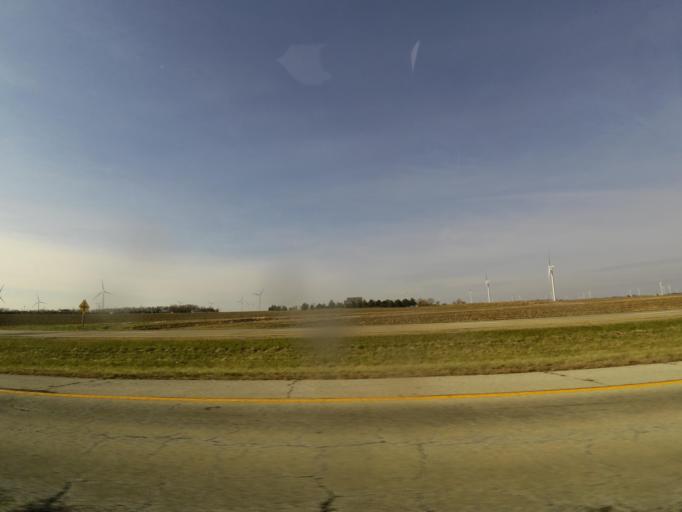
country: US
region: Illinois
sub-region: Macon County
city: Maroa
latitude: 39.9961
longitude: -88.9561
